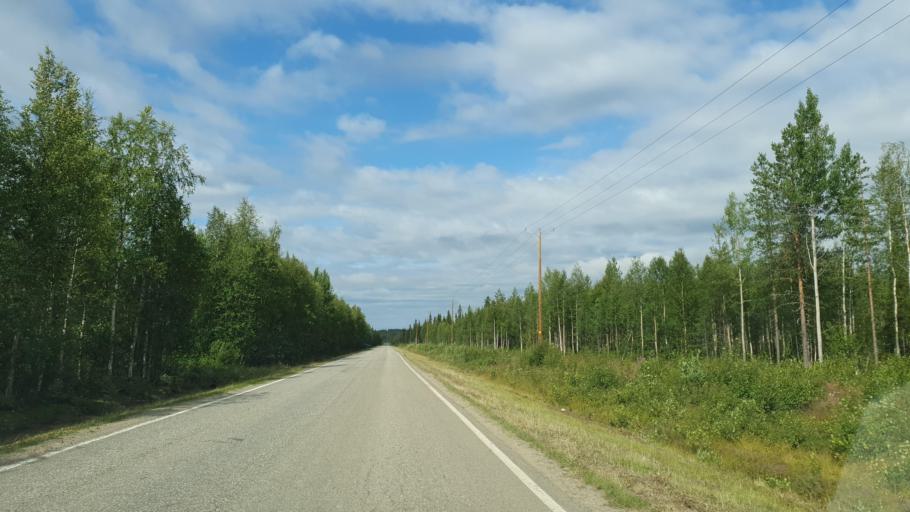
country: FI
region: Lapland
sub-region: Pohjois-Lappi
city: Sodankylae
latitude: 67.5411
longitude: 25.9345
